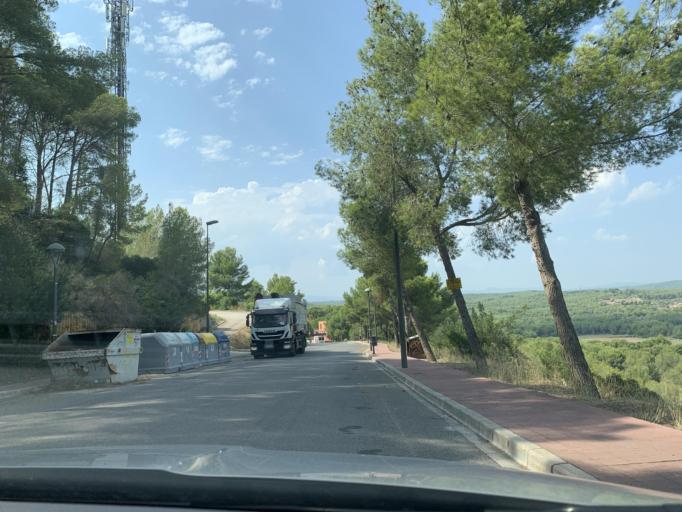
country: ES
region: Catalonia
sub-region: Provincia de Tarragona
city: Altafulla
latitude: 41.1343
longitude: 1.3550
